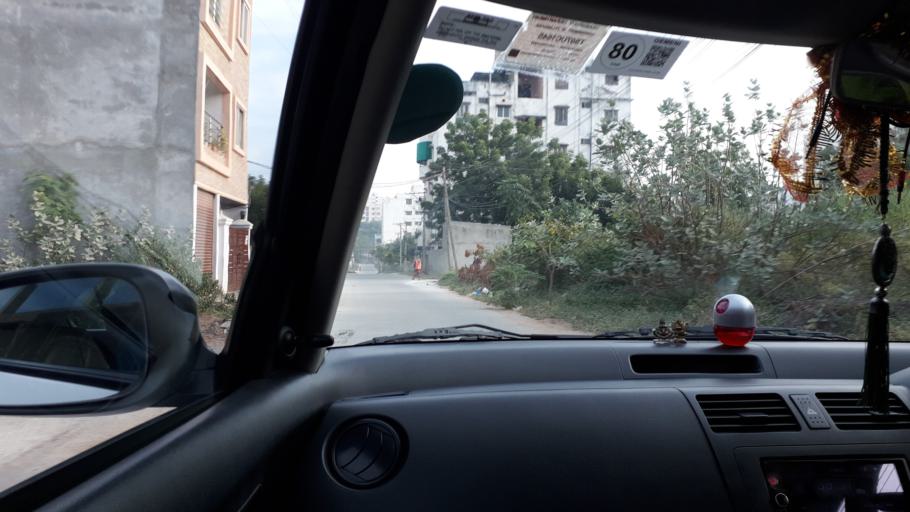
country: IN
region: Telangana
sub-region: Hyderabad
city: Hyderabad
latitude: 17.3920
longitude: 78.3851
